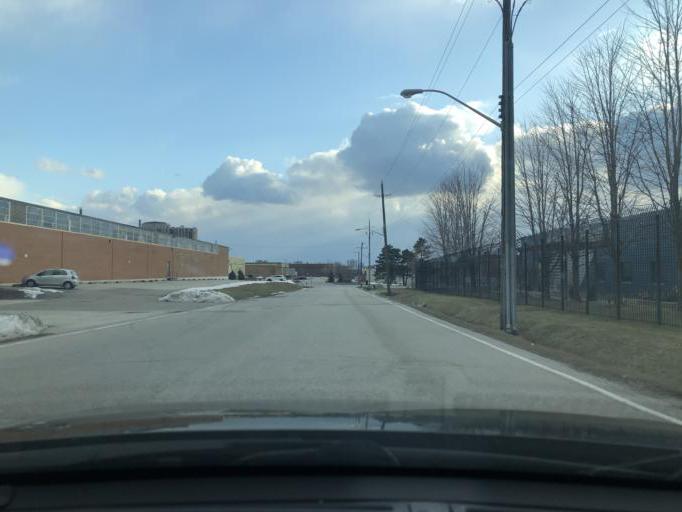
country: CA
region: Ontario
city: Scarborough
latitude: 43.7687
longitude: -79.2942
